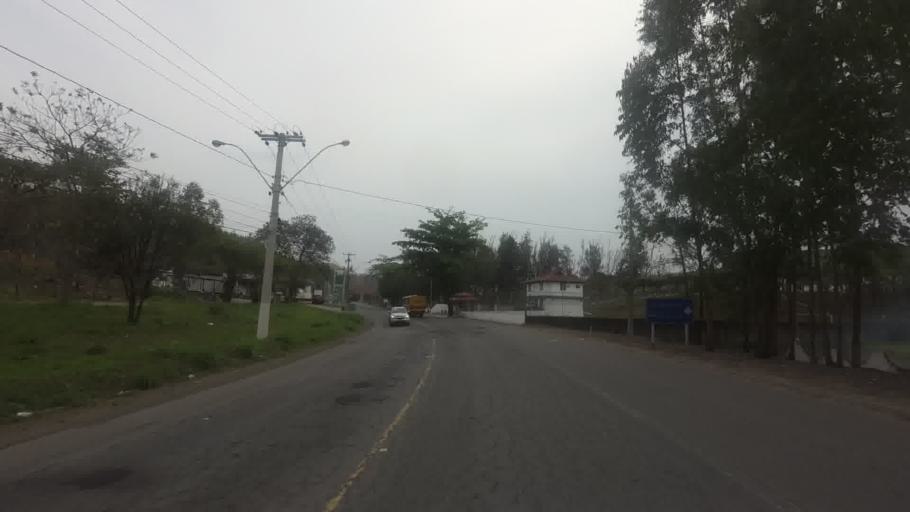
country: BR
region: Rio de Janeiro
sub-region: Santo Antonio De Padua
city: Santo Antonio de Padua
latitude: -21.5611
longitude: -42.1881
